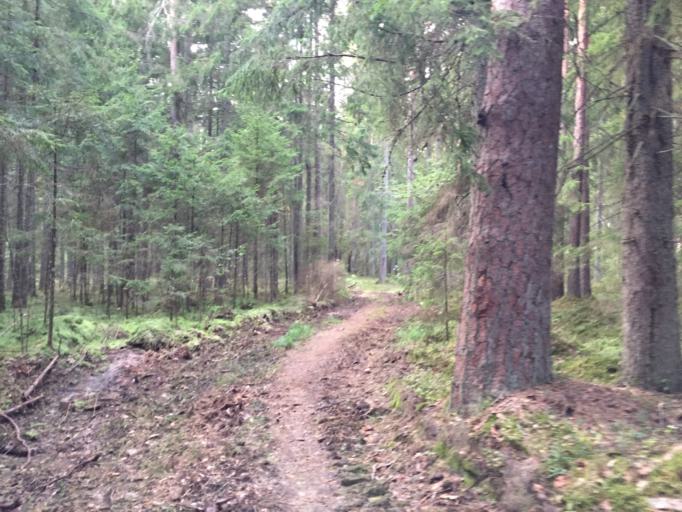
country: LV
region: Baldone
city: Baldone
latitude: 56.7558
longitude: 24.4042
